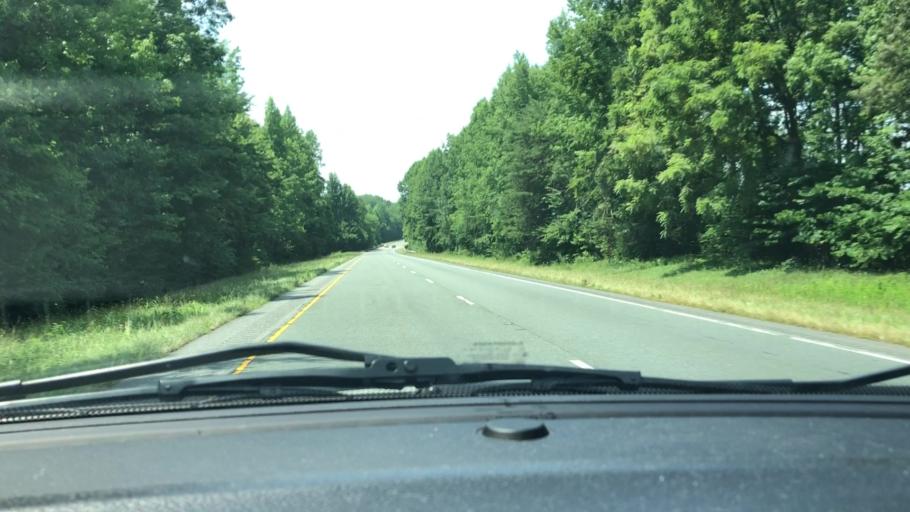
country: US
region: North Carolina
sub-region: Randolph County
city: Liberty
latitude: 35.8610
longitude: -79.6196
